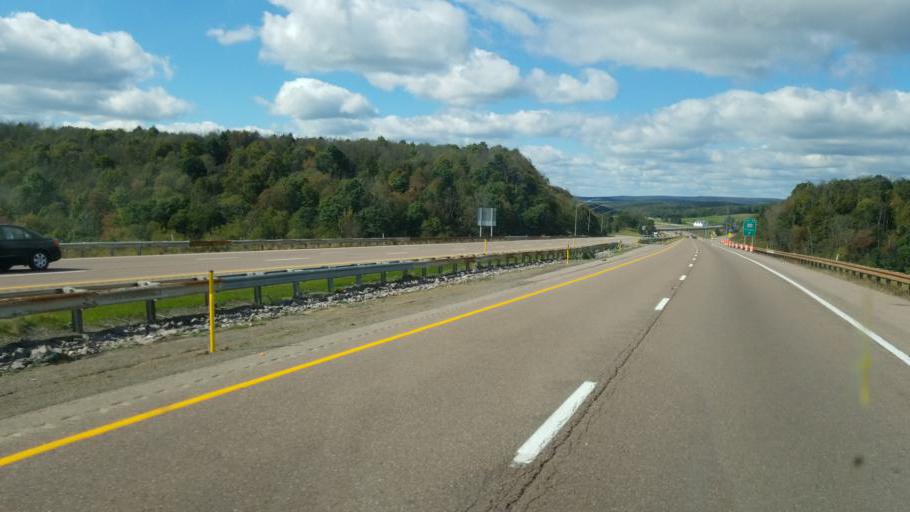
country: US
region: Maryland
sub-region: Allegany County
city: Frostburg
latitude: 39.6782
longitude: -78.9653
